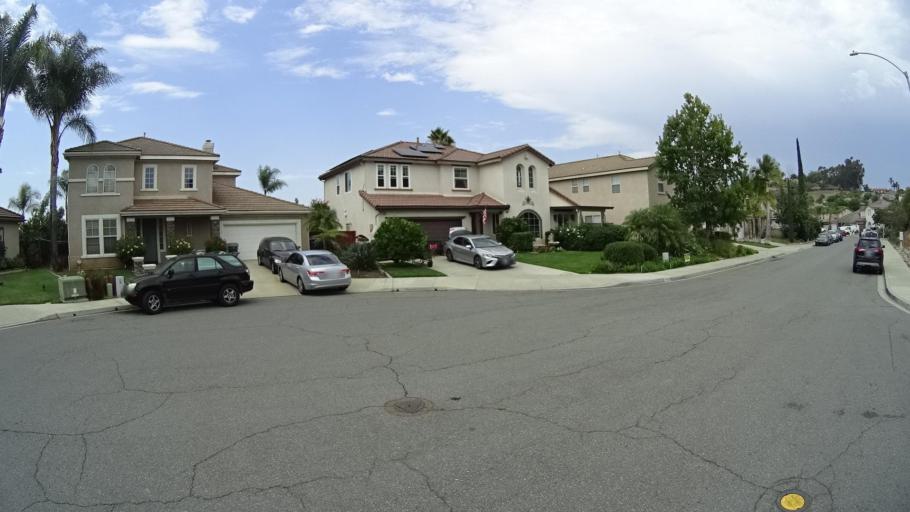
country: US
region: California
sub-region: San Diego County
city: Escondido
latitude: 33.1497
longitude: -117.1130
